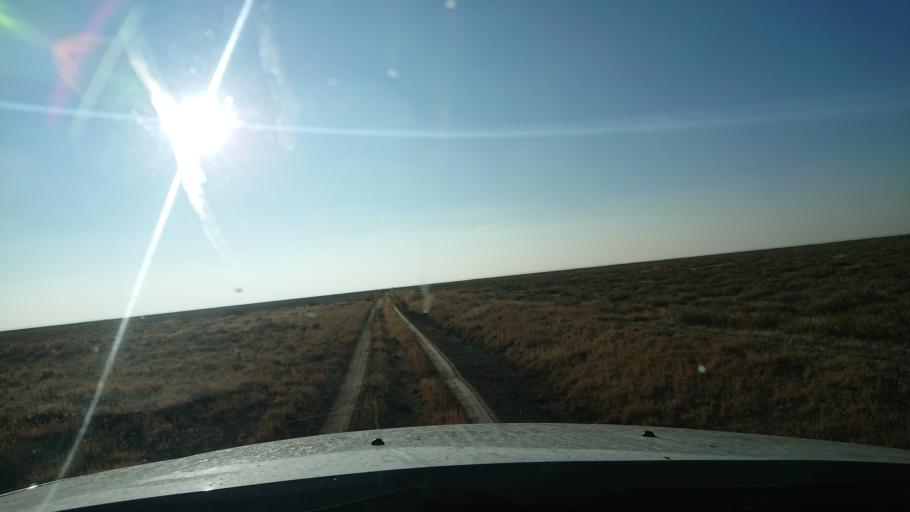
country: TR
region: Aksaray
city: Sultanhani
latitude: 38.3859
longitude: 33.5878
